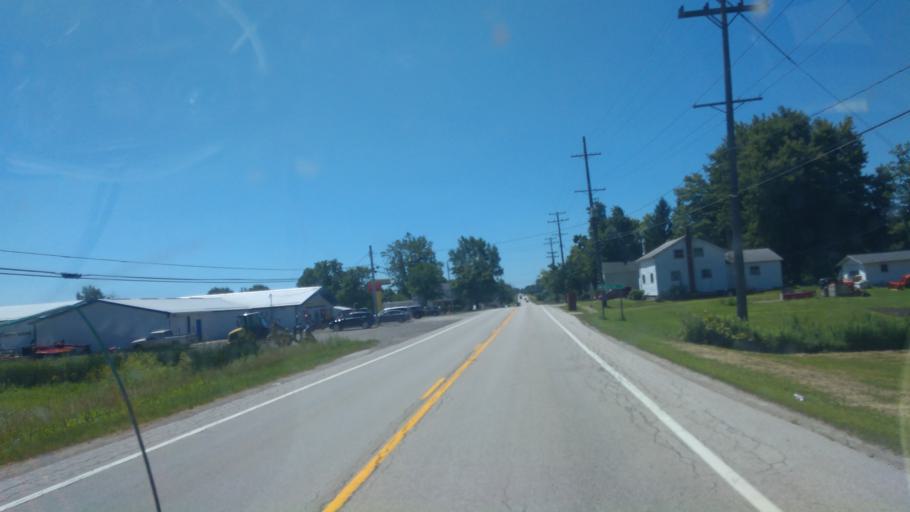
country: US
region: Ohio
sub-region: Ashtabula County
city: Conneaut
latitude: 41.8653
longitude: -80.5725
